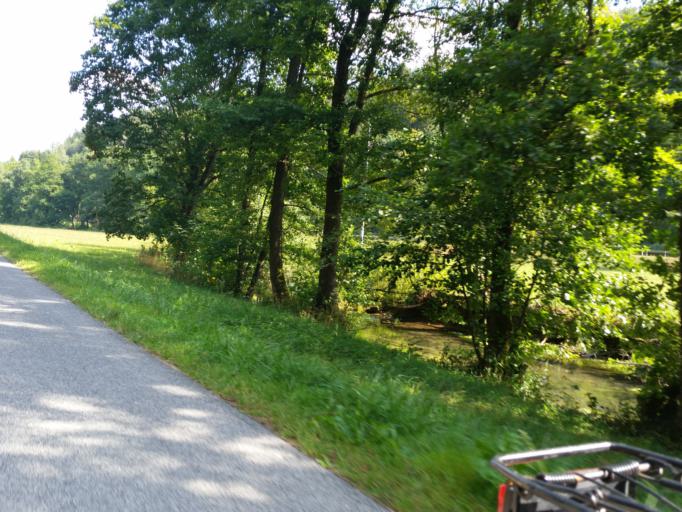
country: DE
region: Bavaria
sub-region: Upper Palatinate
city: Kastl
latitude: 49.3706
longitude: 11.6668
